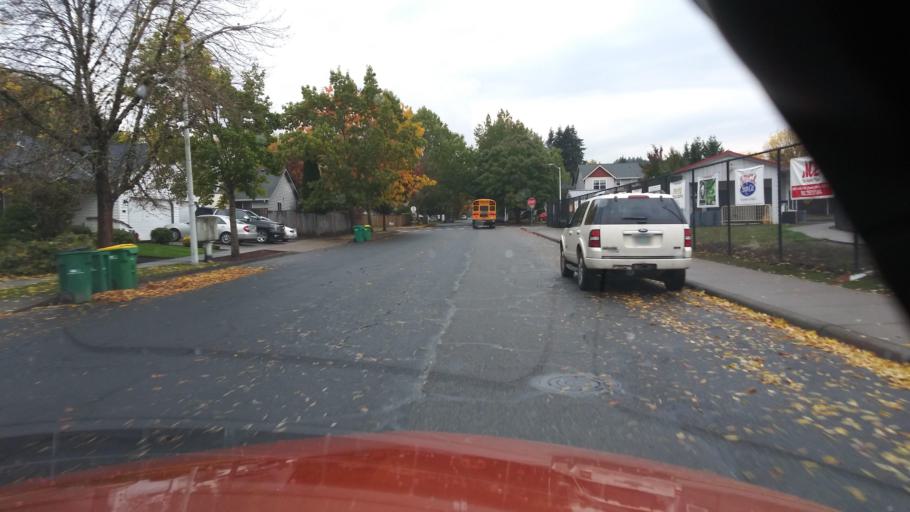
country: US
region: Oregon
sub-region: Washington County
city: Forest Grove
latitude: 45.5338
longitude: -123.1231
